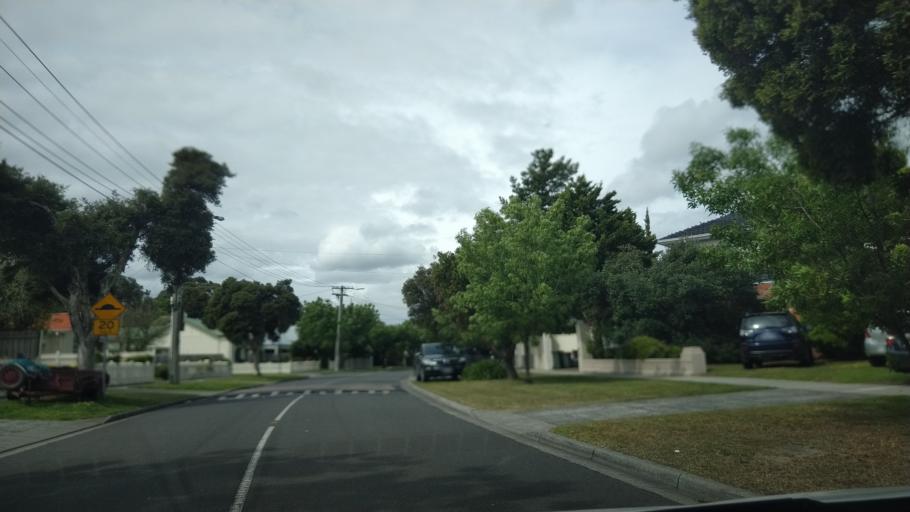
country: AU
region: Victoria
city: Hughesdale
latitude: -37.8974
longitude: 145.0786
